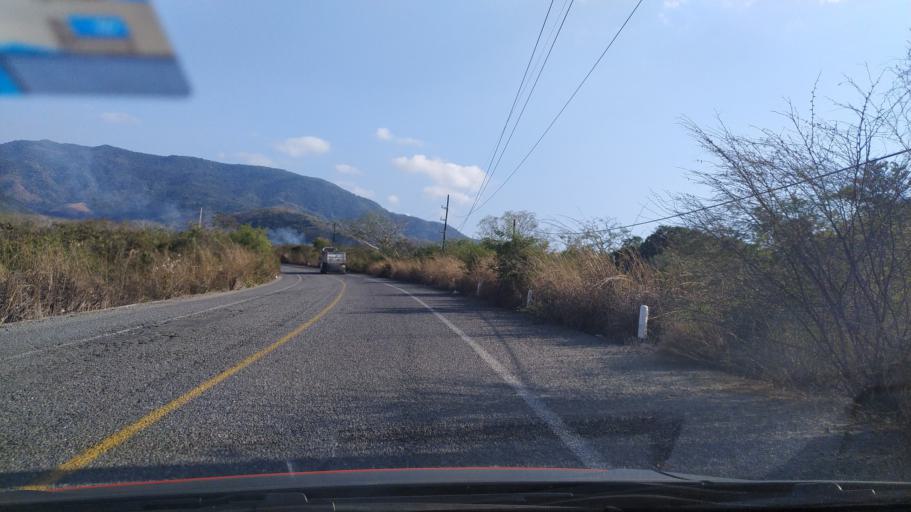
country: MX
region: Michoacan
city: Coahuayana Viejo
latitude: 18.6455
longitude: -103.6734
